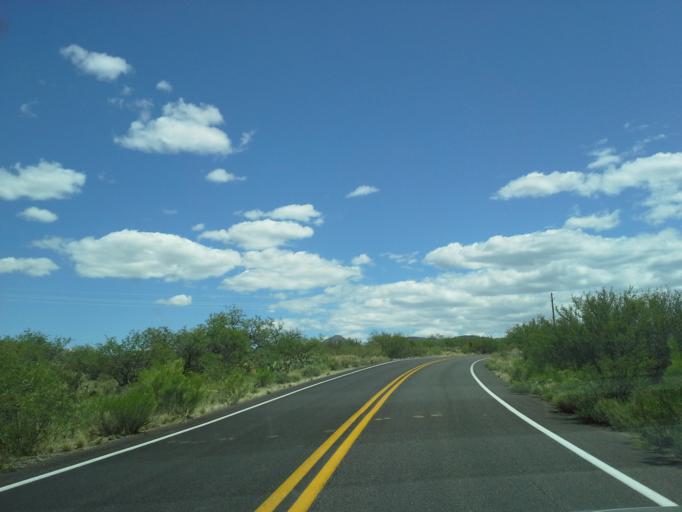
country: US
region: Arizona
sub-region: Pinal County
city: Oracle
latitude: 32.5892
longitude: -110.8416
